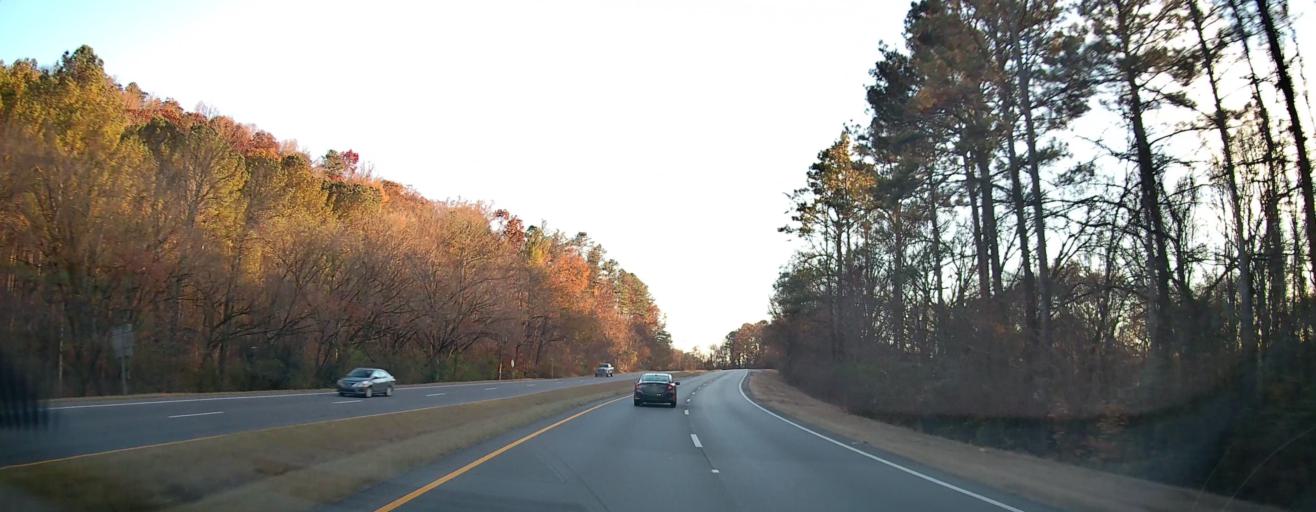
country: US
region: Alabama
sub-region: Etowah County
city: Attalla
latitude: 34.0319
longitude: -86.1103
